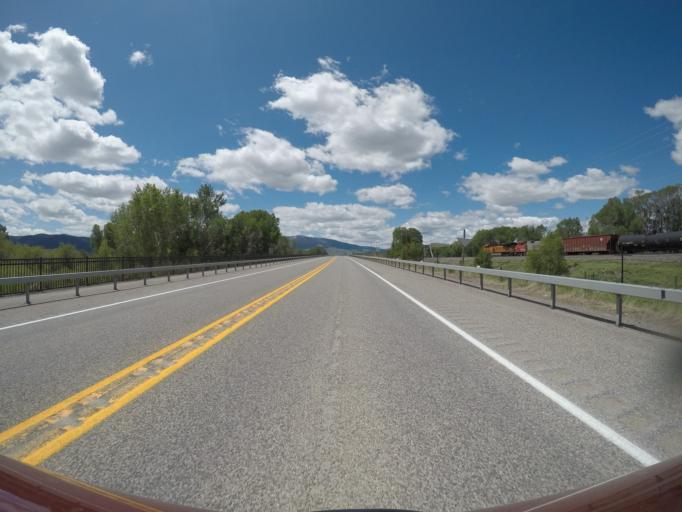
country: US
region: Montana
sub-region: Park County
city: Livingston
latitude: 45.6761
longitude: -110.5341
